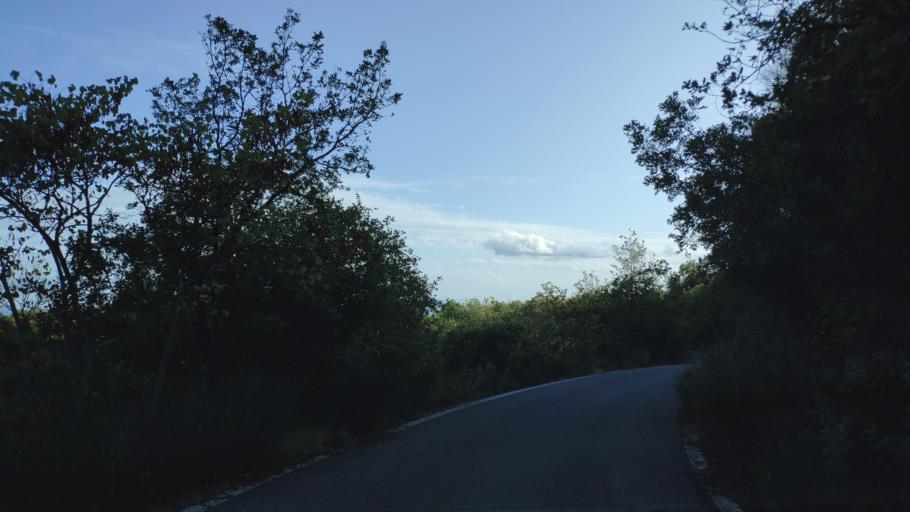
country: GR
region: Peloponnese
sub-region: Nomos Arkadias
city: Dimitsana
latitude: 37.5540
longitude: 22.0411
